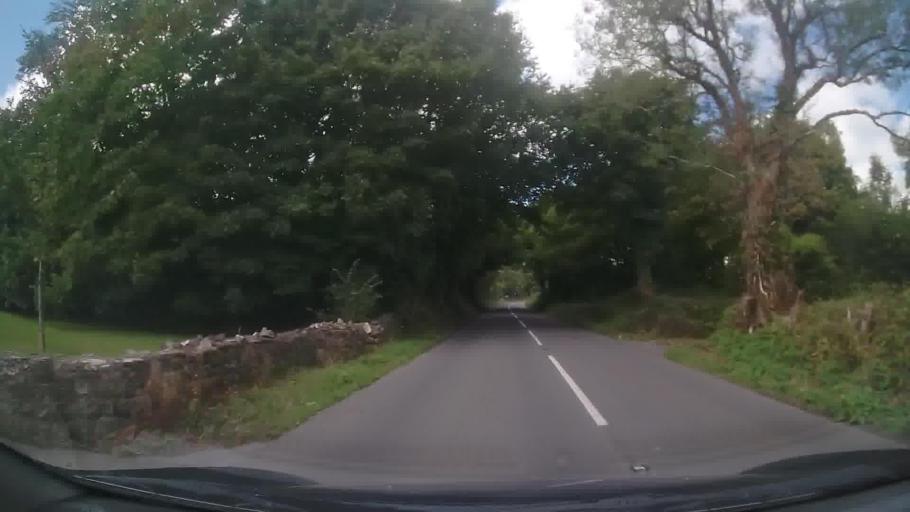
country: GB
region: Wales
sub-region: Pembrokeshire
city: Manorbier
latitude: 51.6512
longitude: -4.7832
